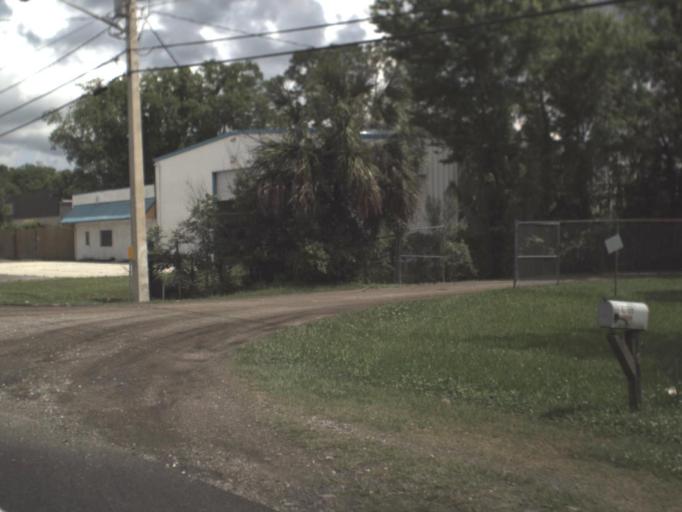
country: US
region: Florida
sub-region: Nassau County
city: Nassau Village-Ratliff
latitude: 30.4195
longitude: -81.7519
